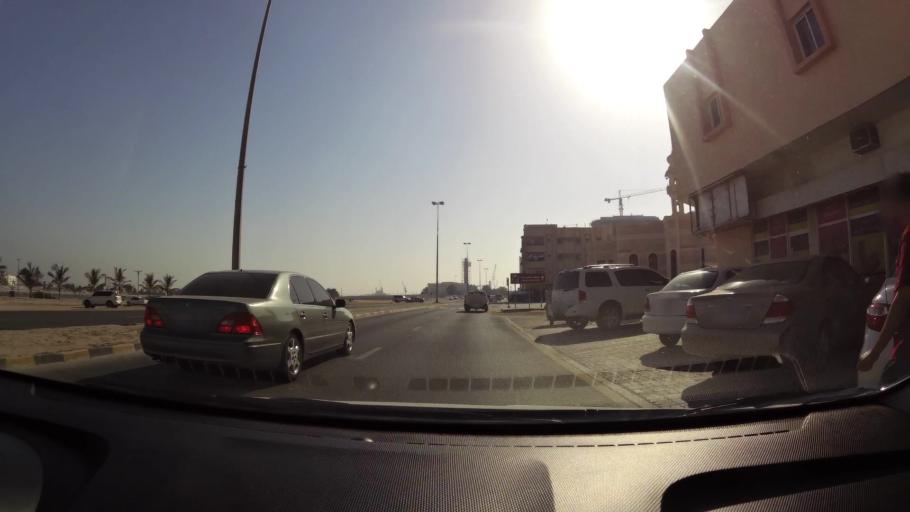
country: AE
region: Ajman
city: Ajman
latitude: 25.4184
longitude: 55.4453
